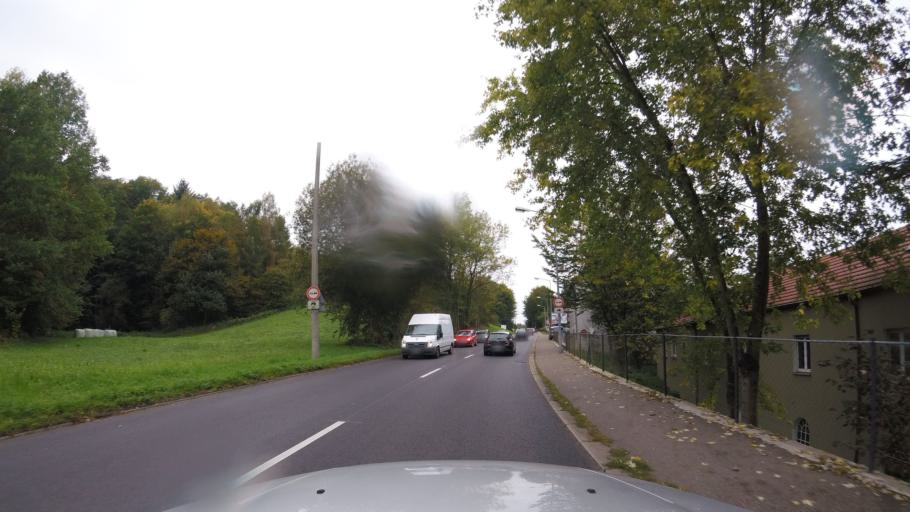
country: DE
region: Baden-Wuerttemberg
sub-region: Regierungsbezirk Stuttgart
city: Schwabisch Gmund
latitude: 48.8067
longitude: 9.7987
